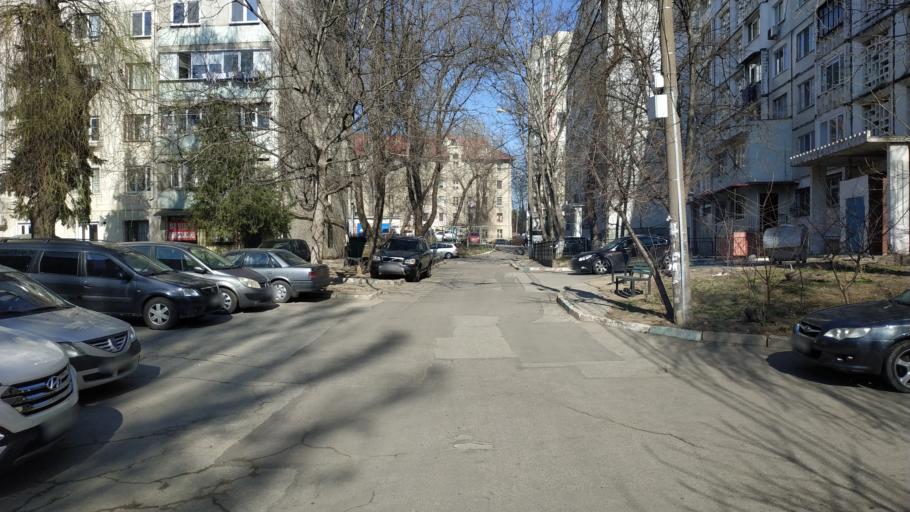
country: MD
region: Chisinau
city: Chisinau
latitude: 47.0285
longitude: 28.8014
